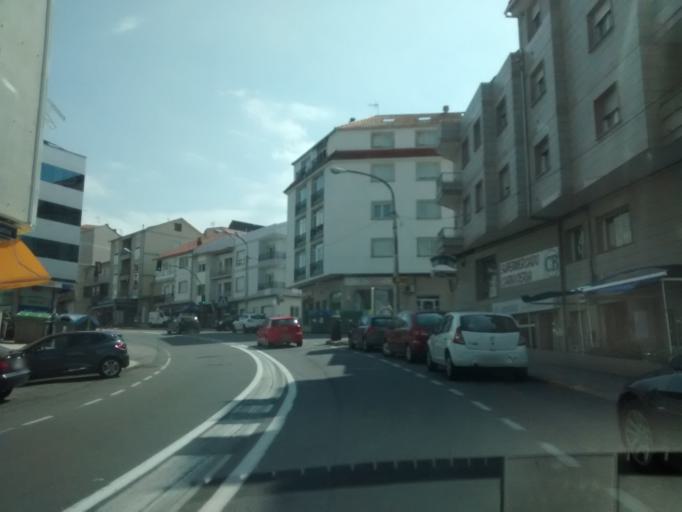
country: ES
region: Galicia
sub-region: Provincia de Pontevedra
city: Sanxenxo
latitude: 42.3959
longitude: -8.8291
